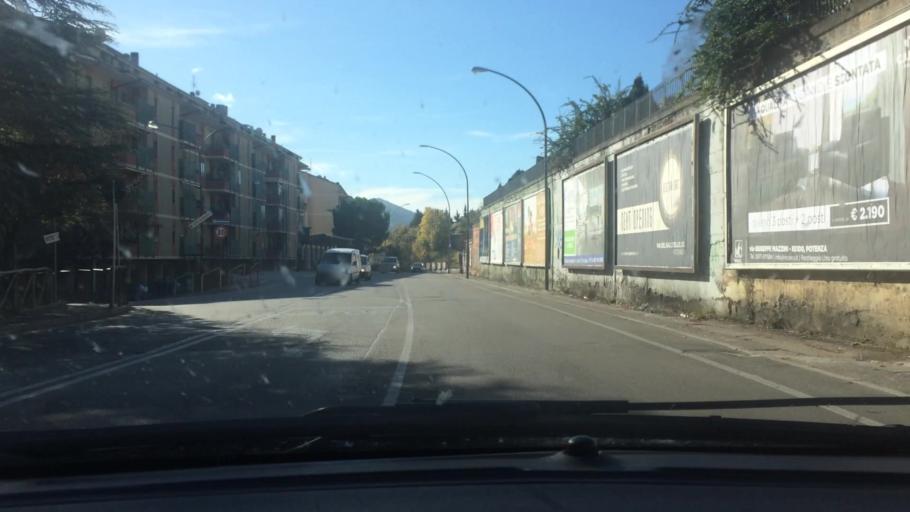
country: IT
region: Basilicate
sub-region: Provincia di Potenza
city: Potenza
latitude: 40.6454
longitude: 15.7954
